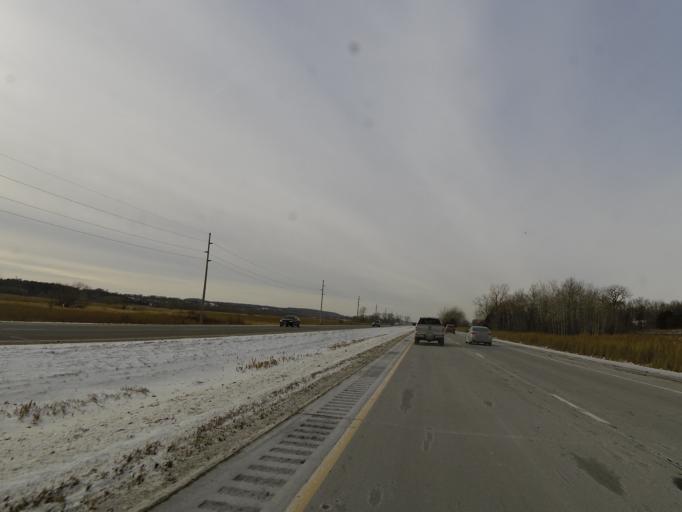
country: US
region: Minnesota
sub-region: Scott County
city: Jordan
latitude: 44.6653
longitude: -93.6541
